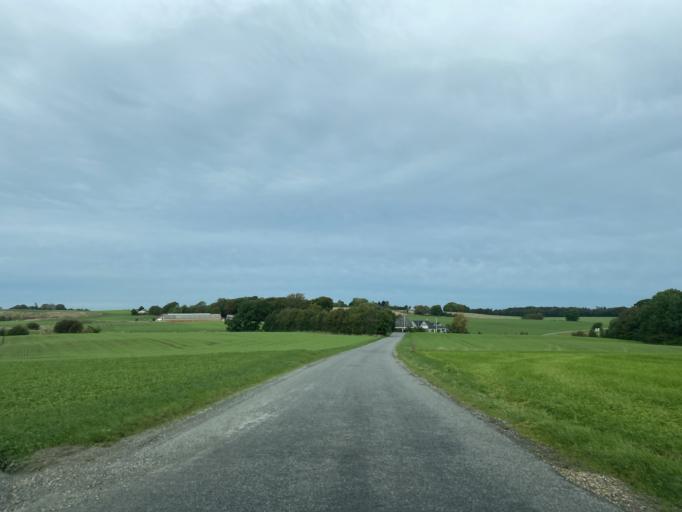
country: DK
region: Central Jutland
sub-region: Silkeborg Kommune
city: Svejbaek
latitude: 56.2312
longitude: 9.6460
